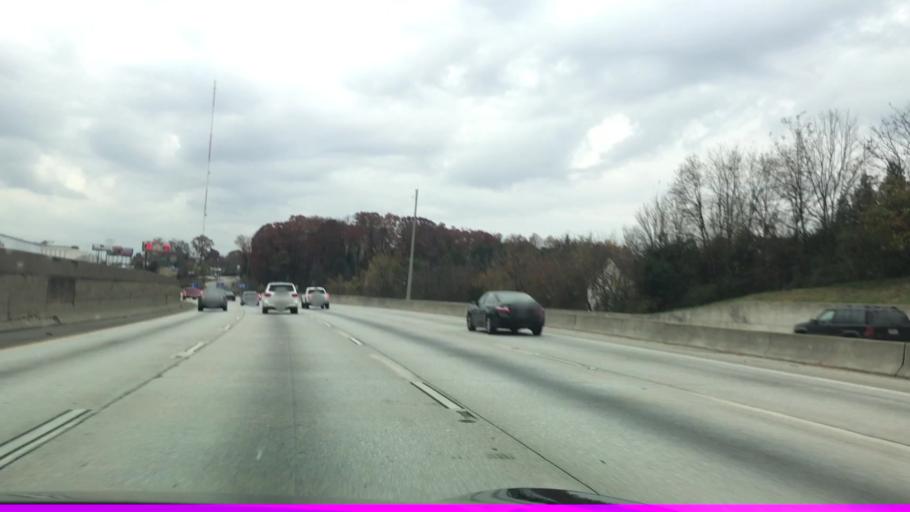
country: US
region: Georgia
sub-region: DeKalb County
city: Scottdale
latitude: 33.7828
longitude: -84.2455
